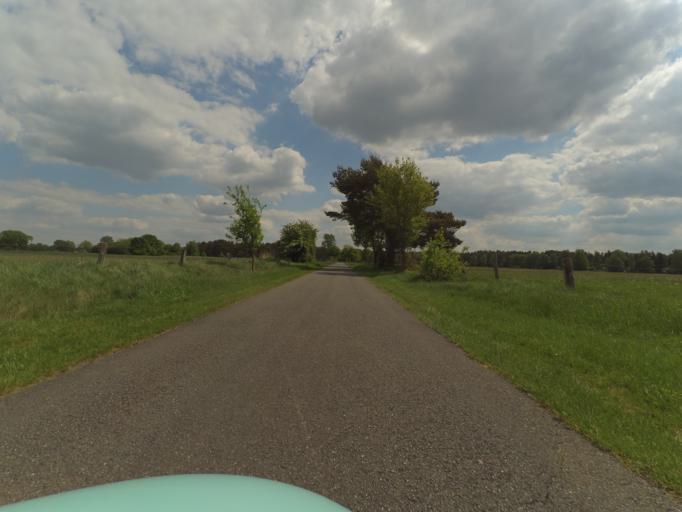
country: DE
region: Lower Saxony
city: Wietze
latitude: 52.6669
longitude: 9.7790
